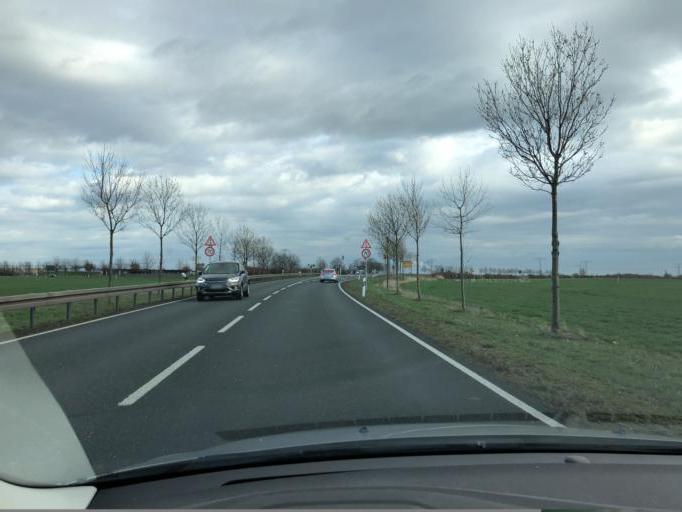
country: DE
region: Saxony
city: Markranstadt
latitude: 51.2772
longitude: 12.2612
